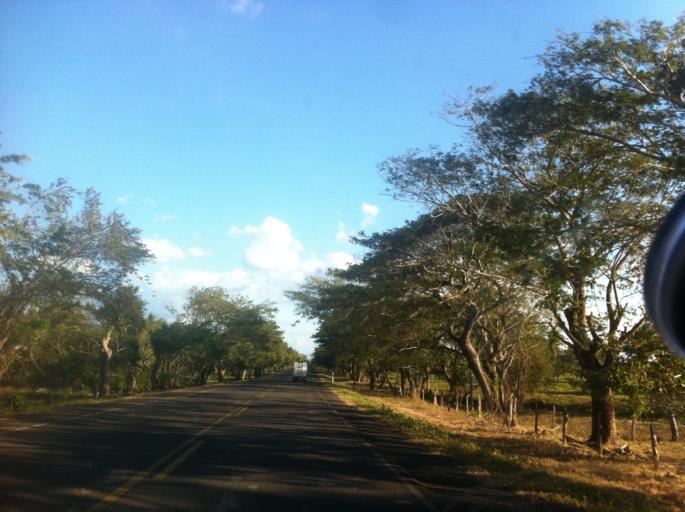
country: NI
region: Rio San Juan
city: Morrito
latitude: 11.6798
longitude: -84.9300
